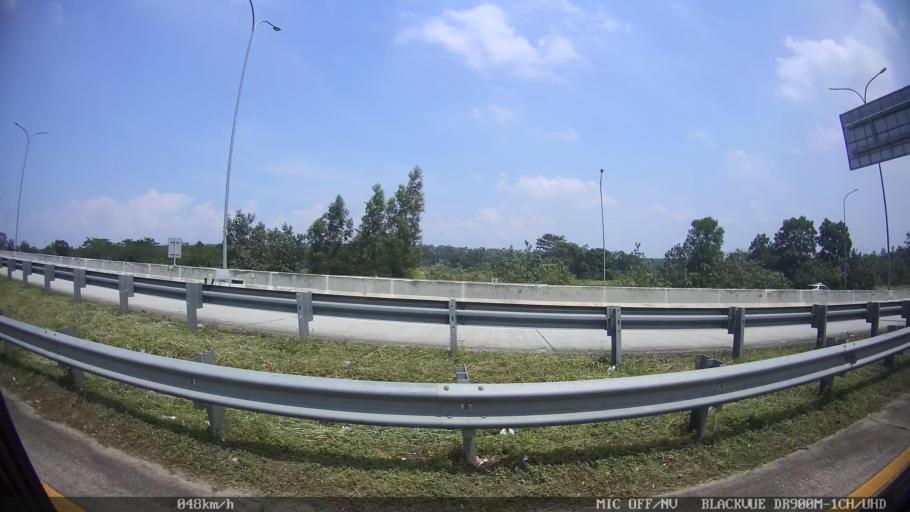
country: ID
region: Lampung
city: Kedaton
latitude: -5.3650
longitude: 105.3275
